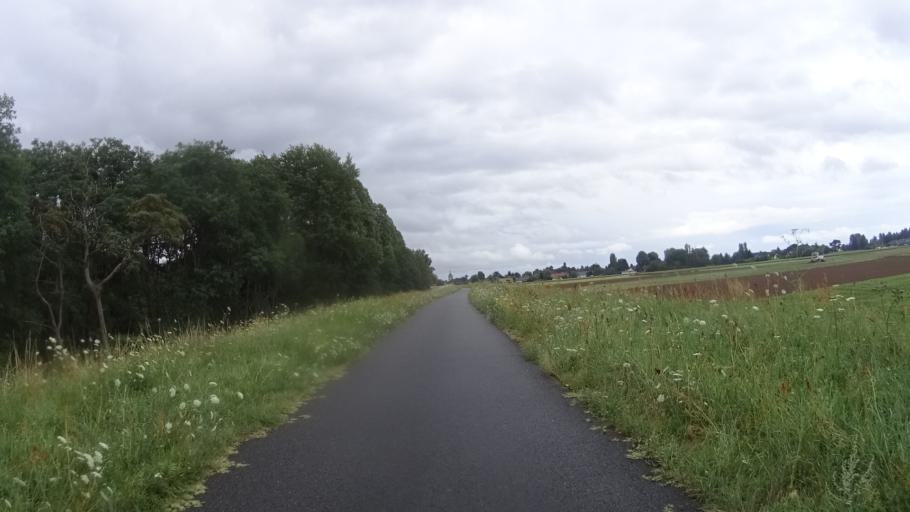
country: FR
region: Centre
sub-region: Departement du Loiret
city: Darvoy
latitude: 47.8692
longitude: 2.1023
